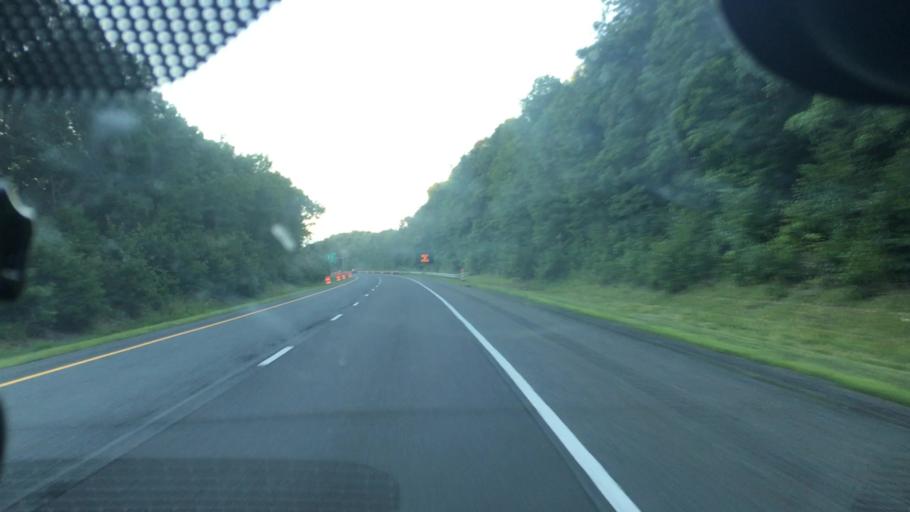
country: US
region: Massachusetts
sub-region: Franklin County
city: Greenfield
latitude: 42.5484
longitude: -72.6213
